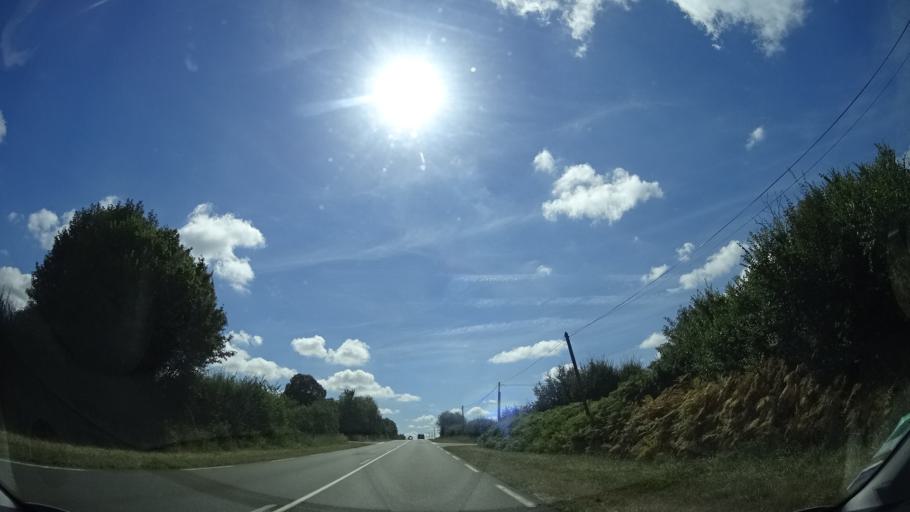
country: FR
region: Pays de la Loire
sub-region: Departement de la Sarthe
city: Auvers-le-Hamon
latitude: 47.9077
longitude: -0.4523
